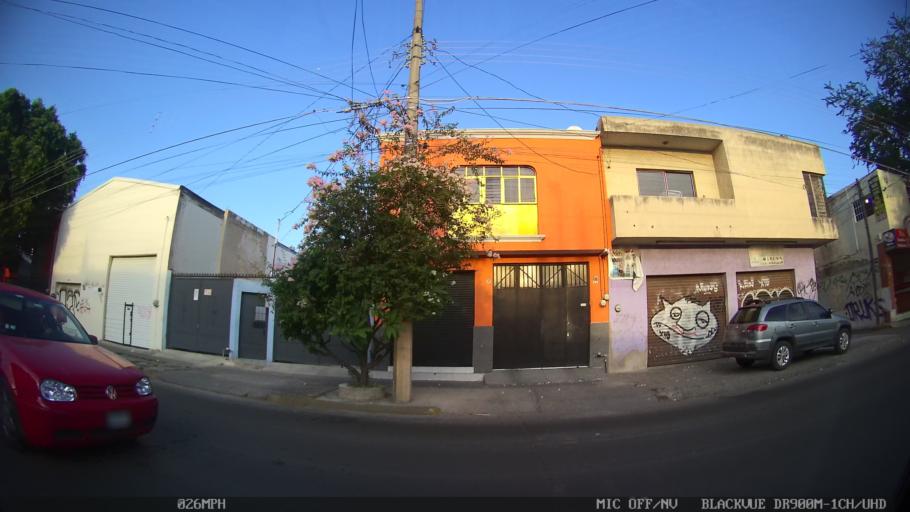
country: MX
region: Jalisco
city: Tlaquepaque
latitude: 20.6639
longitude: -103.3167
